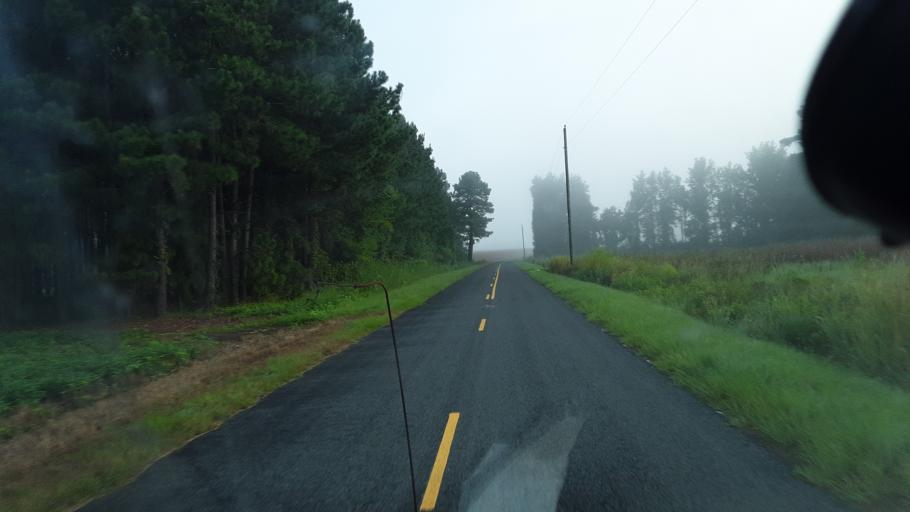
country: US
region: South Carolina
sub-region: Williamsburg County
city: Kingstree
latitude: 33.8033
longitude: -79.9643
